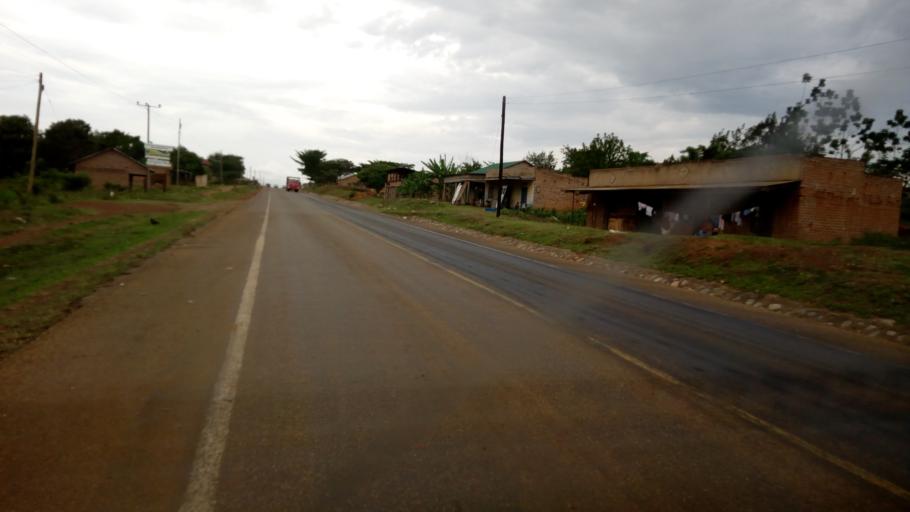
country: UG
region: Eastern Region
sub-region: Mbale District
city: Mbale
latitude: 0.9251
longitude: 34.1603
